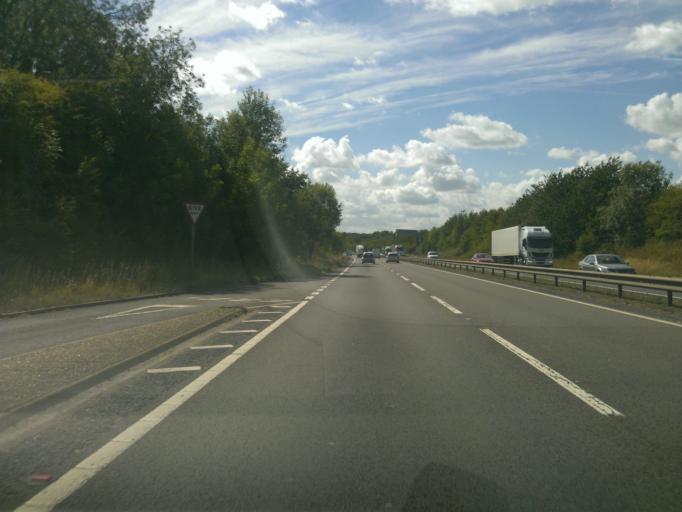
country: GB
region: England
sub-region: Northamptonshire
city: Thrapston
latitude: 52.3927
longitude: -0.5867
